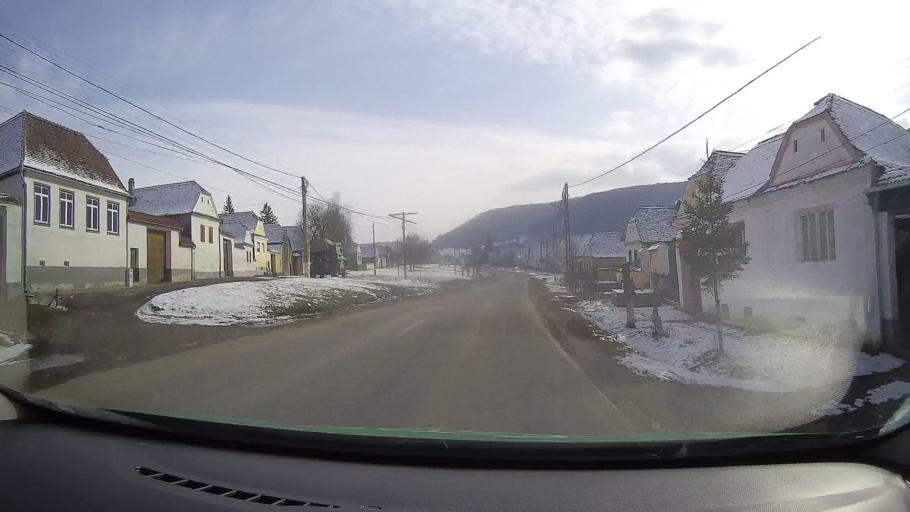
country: RO
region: Mures
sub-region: Comuna Apold
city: Saes
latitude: 46.1528
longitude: 24.7705
